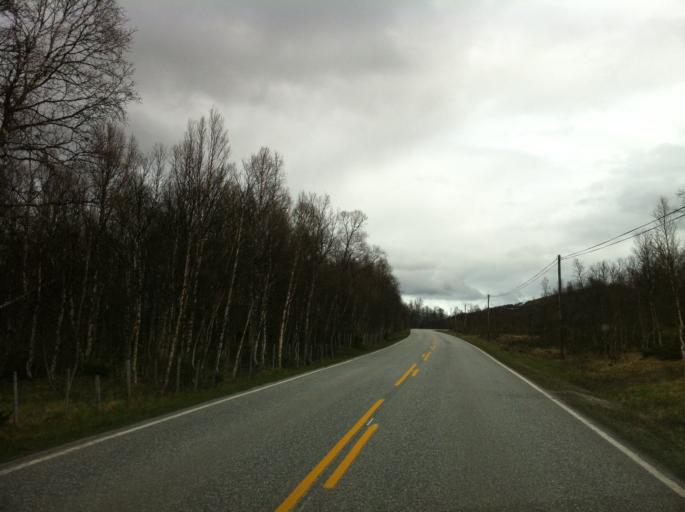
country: NO
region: Sor-Trondelag
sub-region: Roros
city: Roros
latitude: 62.6120
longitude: 11.6072
